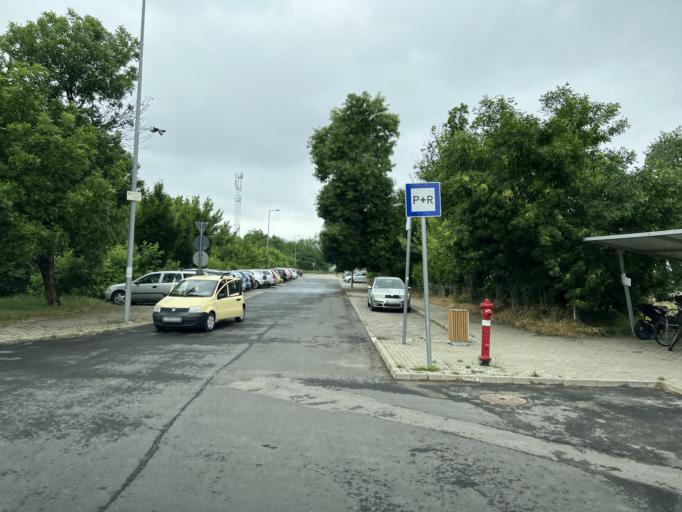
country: HU
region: Pest
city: Tura
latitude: 47.6261
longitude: 19.5970
